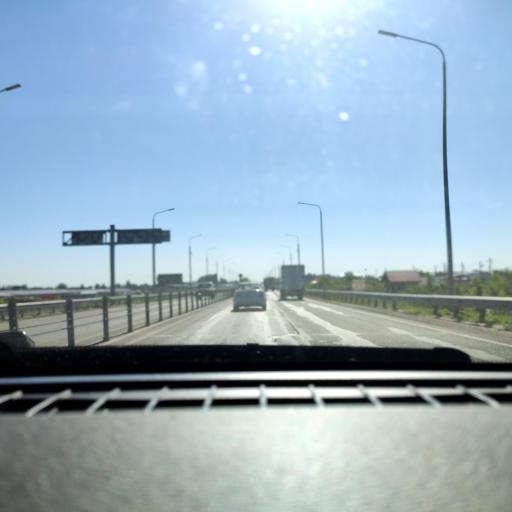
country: RU
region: Voronezj
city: Somovo
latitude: 51.6781
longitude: 39.3080
